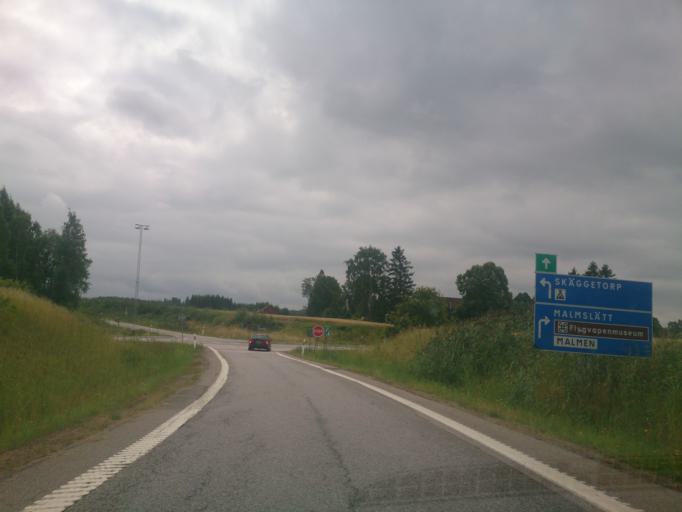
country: SE
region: OEstergoetland
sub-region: Linkopings Kommun
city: Malmslatt
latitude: 58.4260
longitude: 15.5352
